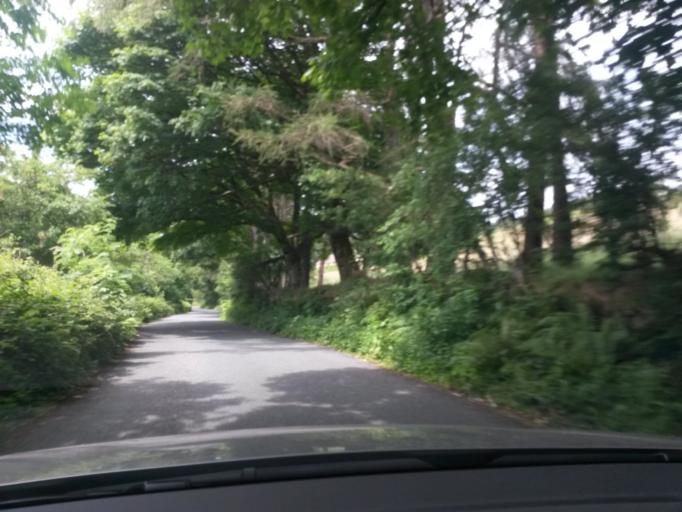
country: IE
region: Leinster
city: Ballinteer
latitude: 53.1993
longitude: -6.2894
